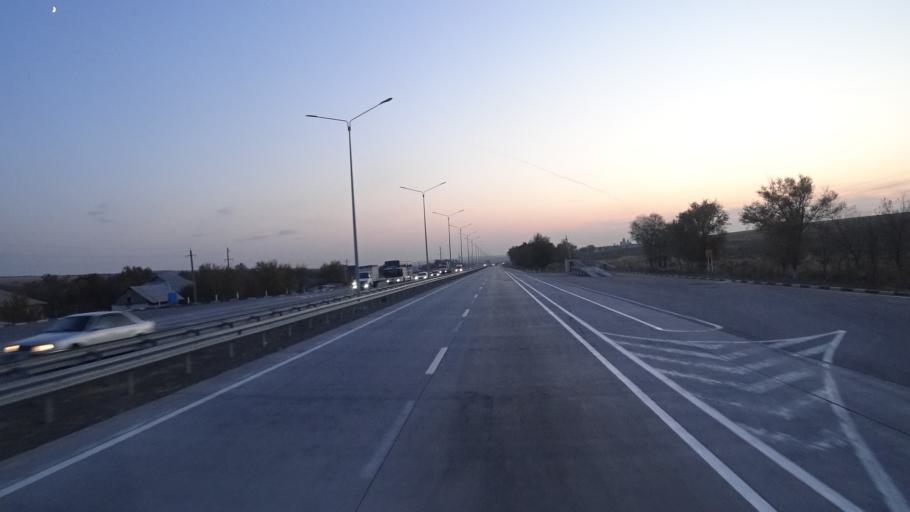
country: KZ
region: Ongtustik Qazaqstan
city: Qazyqurt
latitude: 41.8849
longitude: 69.4411
